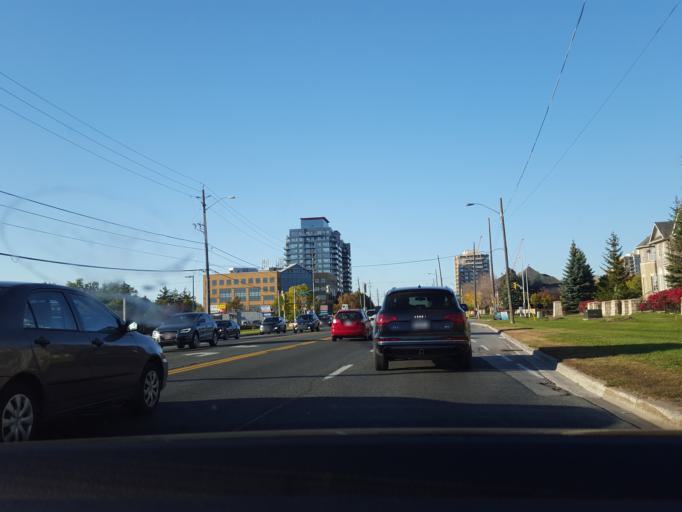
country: CA
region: Ontario
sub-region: York
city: Richmond Hill
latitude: 43.8453
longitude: -79.4310
